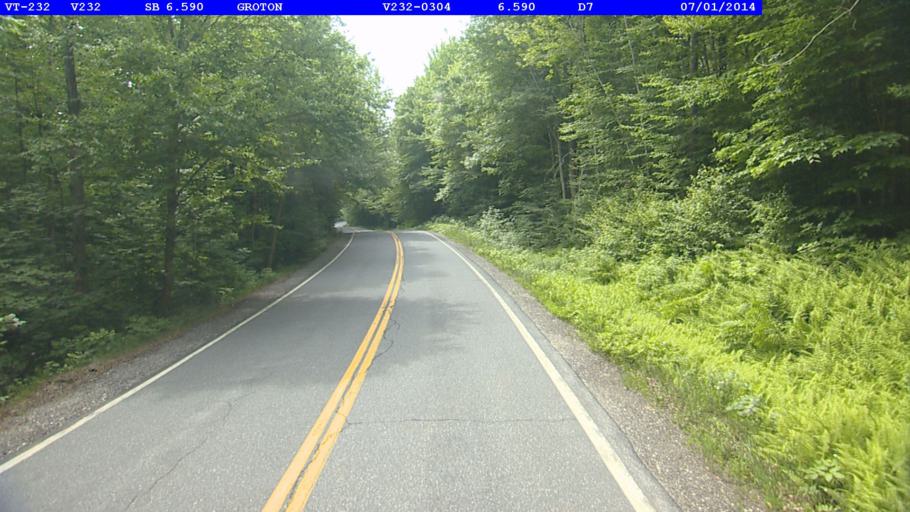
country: US
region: Vermont
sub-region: Washington County
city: Barre
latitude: 44.2892
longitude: -72.3009
